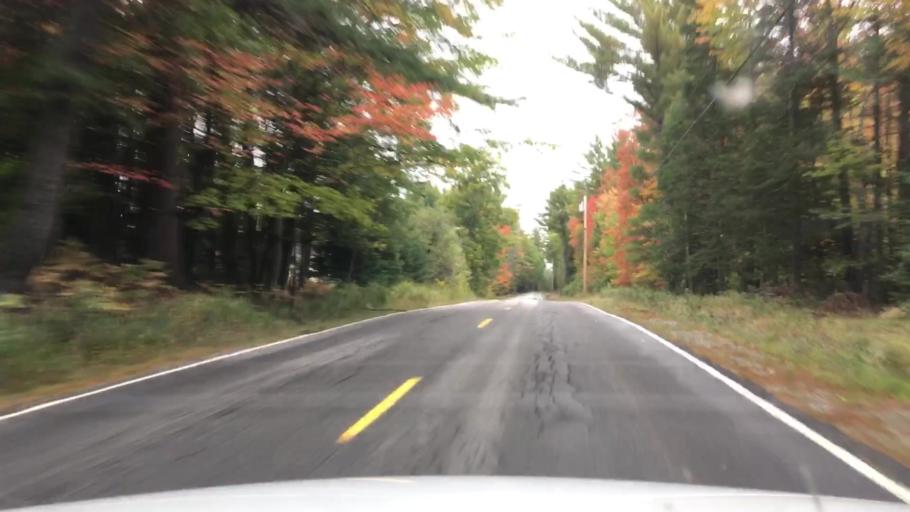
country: US
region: Maine
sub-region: Oxford County
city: Bethel
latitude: 44.3736
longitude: -70.7998
